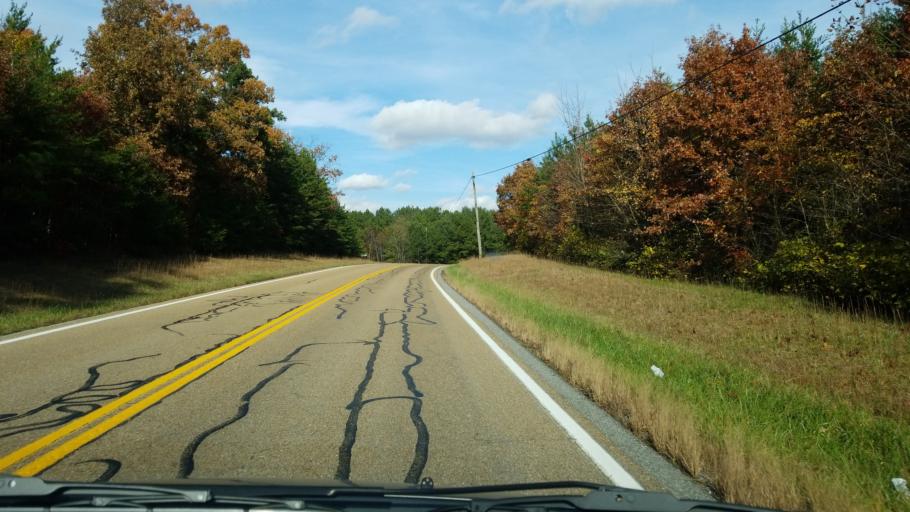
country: US
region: Tennessee
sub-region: Sequatchie County
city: Dunlap
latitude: 35.4562
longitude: -85.4979
